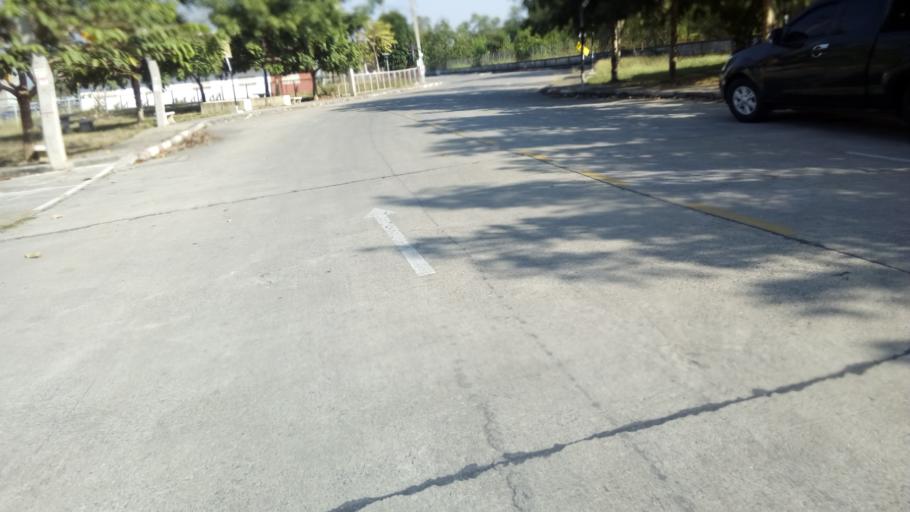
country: TH
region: Pathum Thani
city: Nong Suea
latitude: 14.0562
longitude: 100.8416
